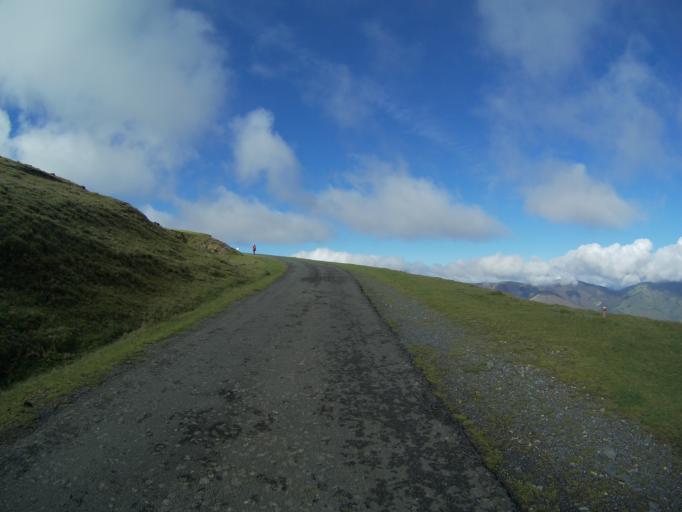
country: ES
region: Navarre
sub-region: Provincia de Navarra
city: Orbara
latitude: 43.0616
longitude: -1.2676
